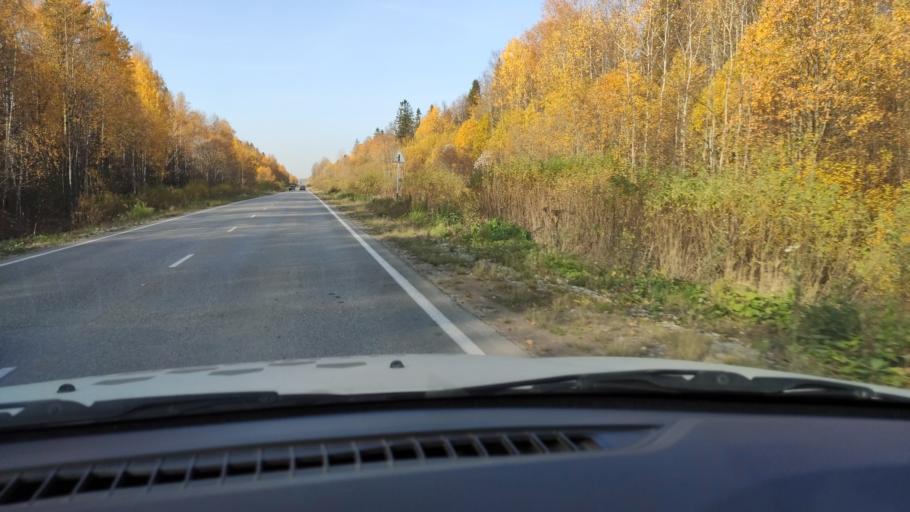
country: RU
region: Perm
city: Novyye Lyady
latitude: 58.0251
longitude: 56.6352
